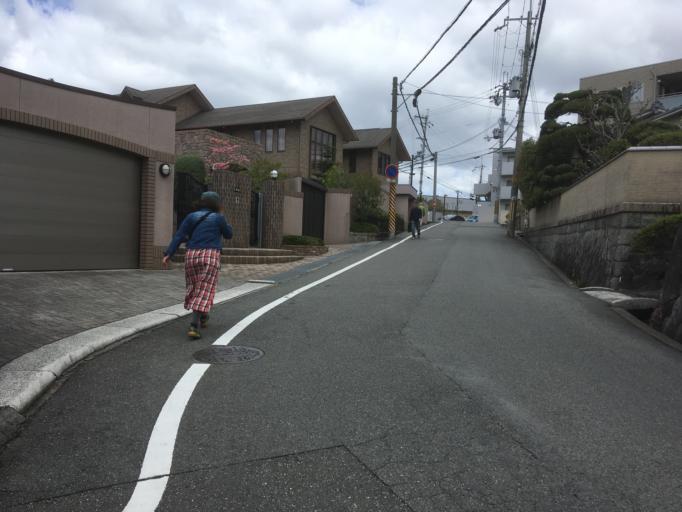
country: JP
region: Nara
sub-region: Ikoma-shi
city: Ikoma
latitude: 34.6956
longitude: 135.6960
